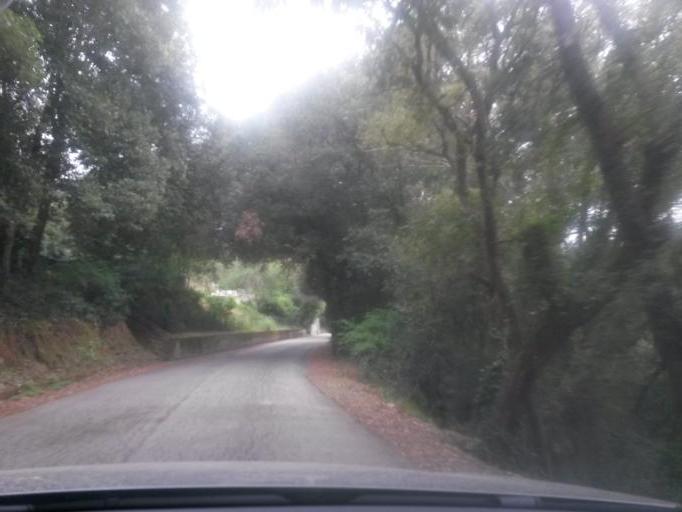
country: IT
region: Tuscany
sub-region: Provincia di Livorno
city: Capoliveri
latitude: 42.7458
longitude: 10.3973
